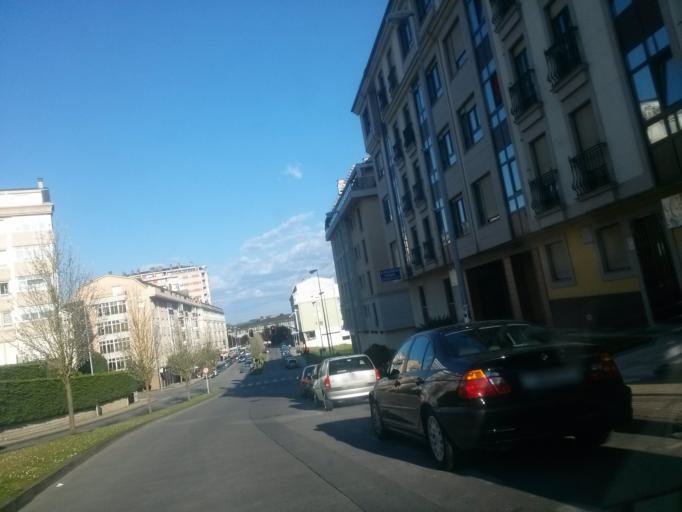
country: ES
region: Galicia
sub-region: Provincia de Lugo
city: Lugo
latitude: 42.9949
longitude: -7.5528
